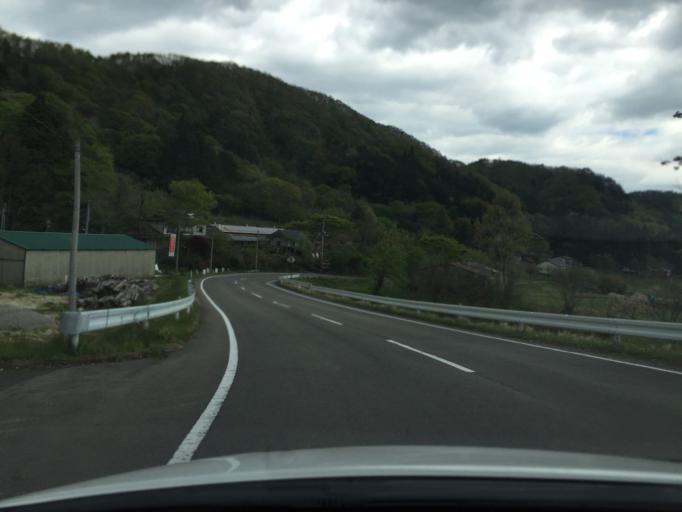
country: JP
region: Fukushima
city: Yanagawamachi-saiwaicho
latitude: 37.7474
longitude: 140.7068
